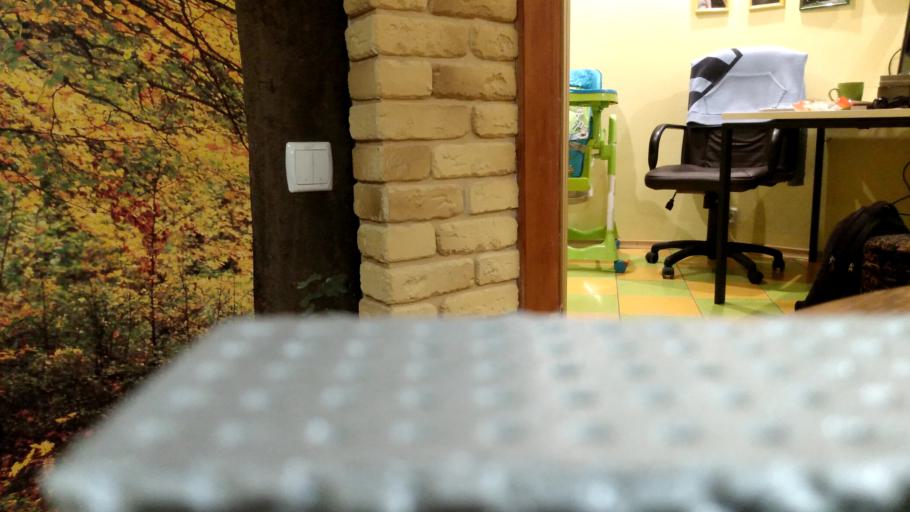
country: RU
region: Republic of Karelia
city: Pudozh
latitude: 61.8325
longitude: 37.6600
